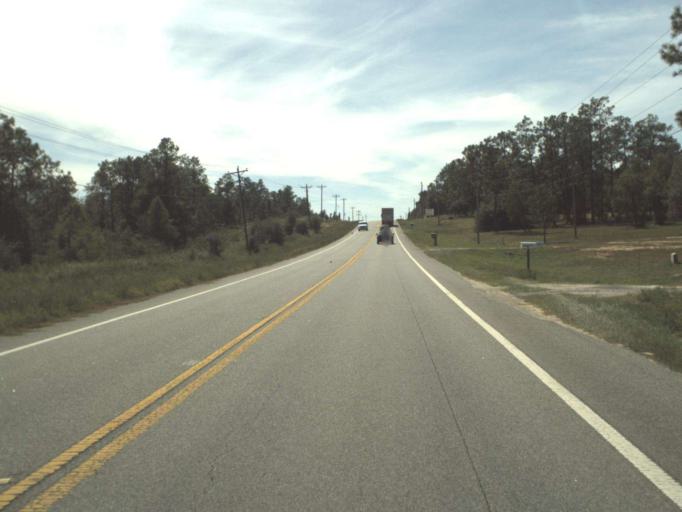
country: US
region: Florida
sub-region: Bay County
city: Youngstown
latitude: 30.5286
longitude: -85.6456
